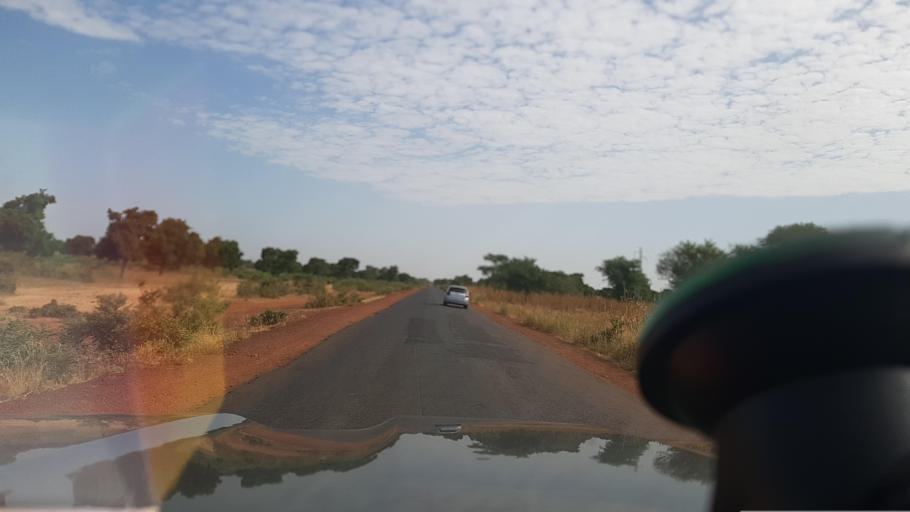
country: ML
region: Segou
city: Segou
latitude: 13.5121
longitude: -6.1417
